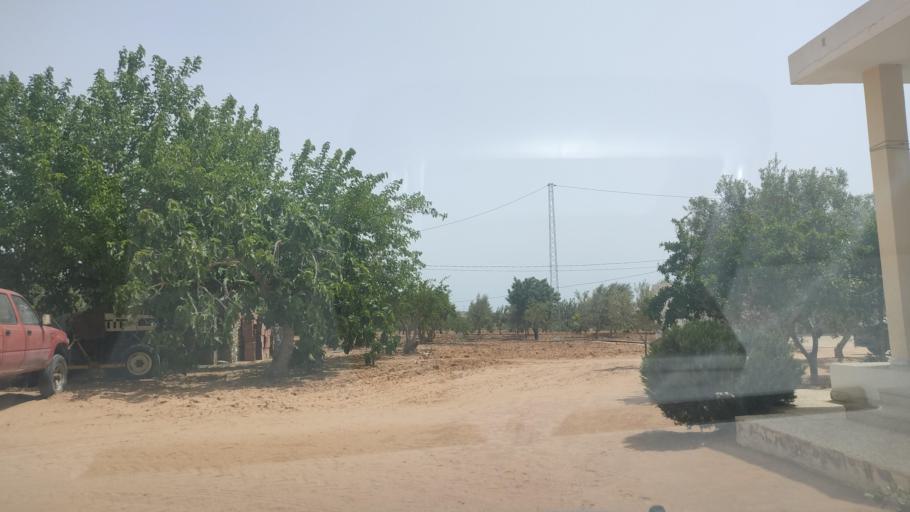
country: TN
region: Safaqis
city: Sfax
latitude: 34.8432
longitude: 10.5871
